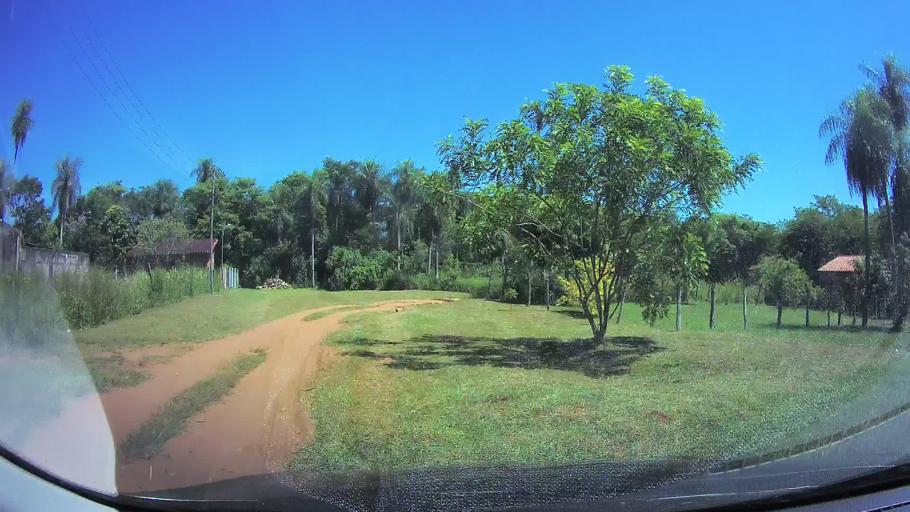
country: PY
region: Central
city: Aregua
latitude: -25.3314
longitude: -57.3968
